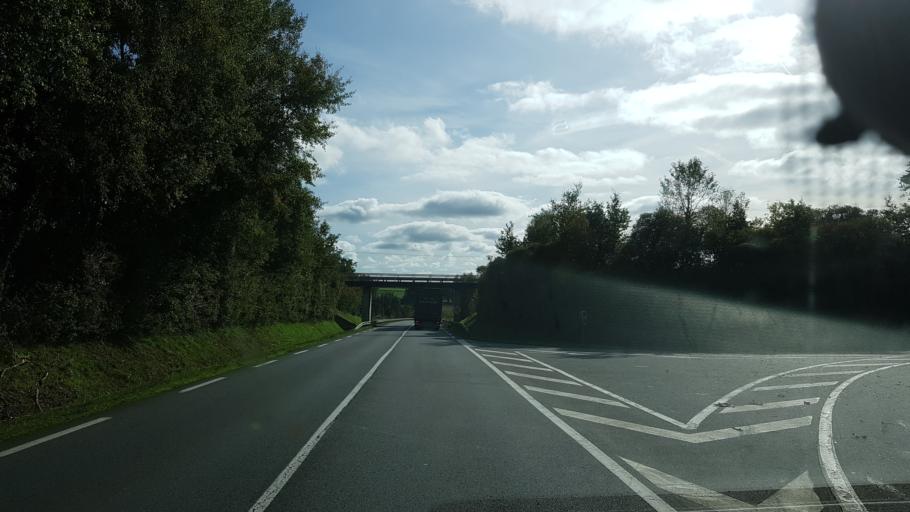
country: FR
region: Poitou-Charentes
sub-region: Departement de la Charente
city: Confolens
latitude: 46.0524
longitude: 0.6670
